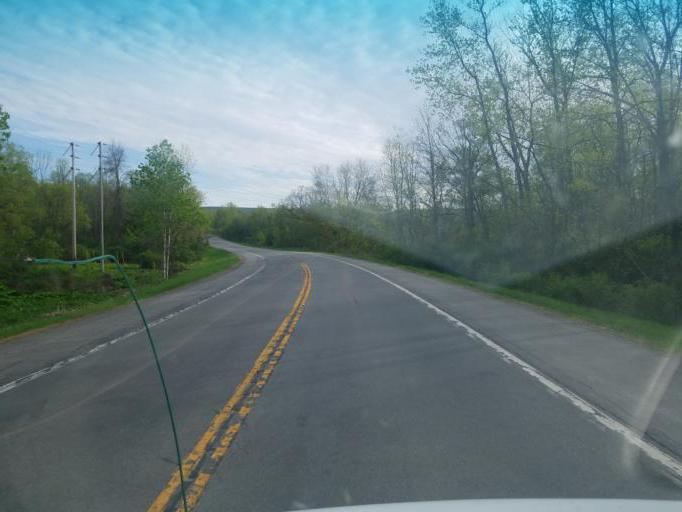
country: US
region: New York
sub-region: Herkimer County
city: Little Falls
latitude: 43.0254
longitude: -74.8758
